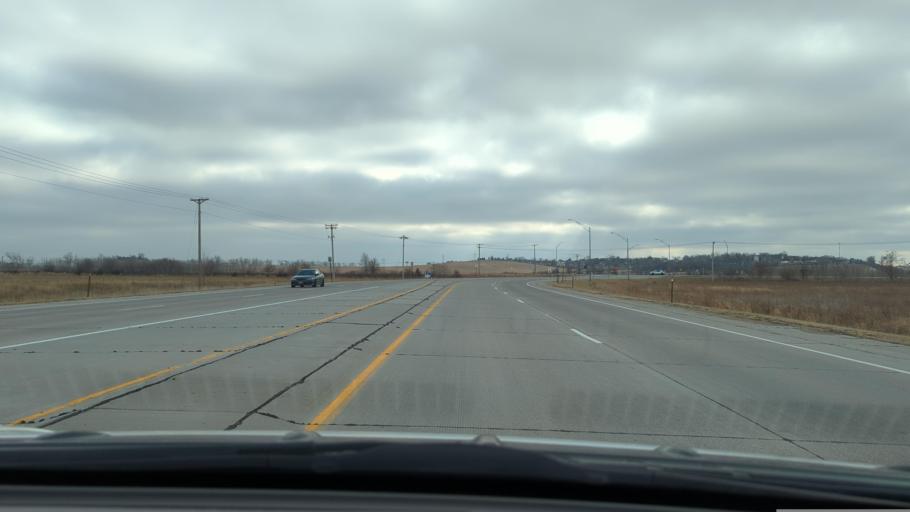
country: US
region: Nebraska
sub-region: Sarpy County
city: Offutt Air Force Base
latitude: 41.1061
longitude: -95.9272
